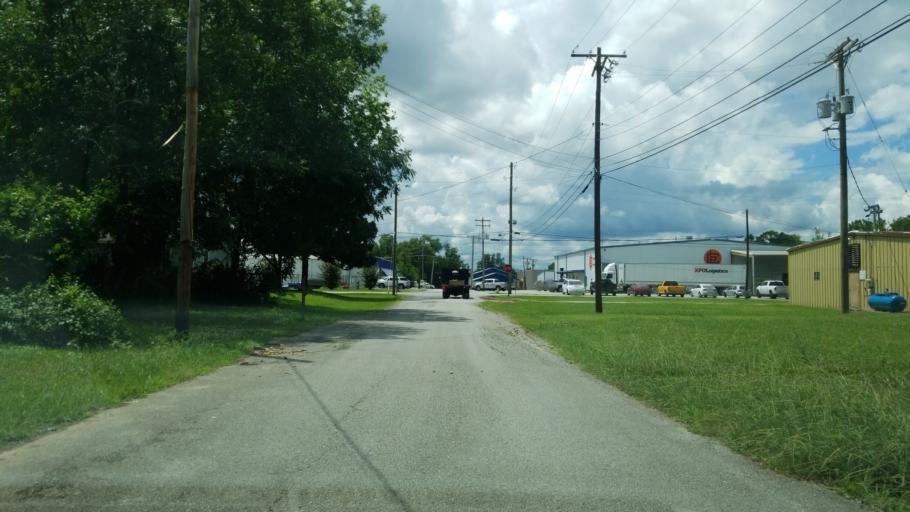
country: US
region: Tennessee
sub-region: Hamilton County
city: East Chattanooga
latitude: 35.0758
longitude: -85.2553
